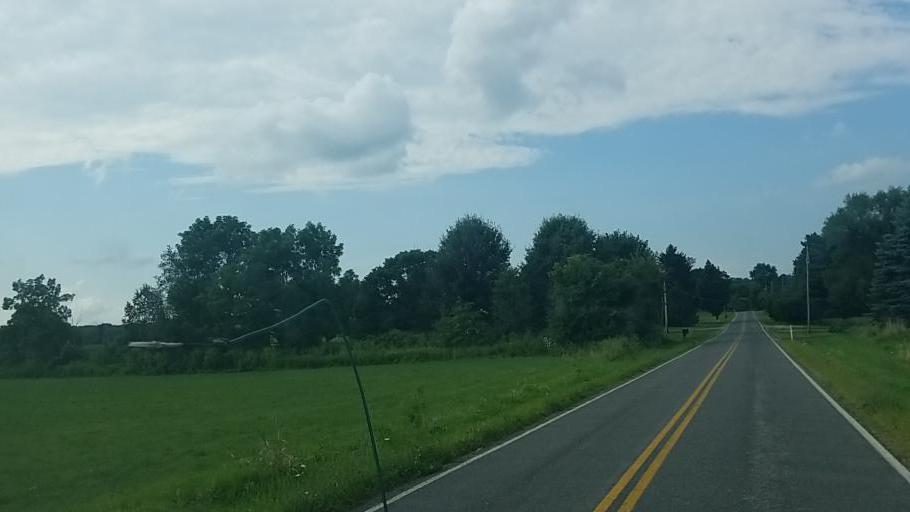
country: US
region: Ohio
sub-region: Medina County
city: Westfield Center
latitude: 41.0143
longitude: -81.9412
